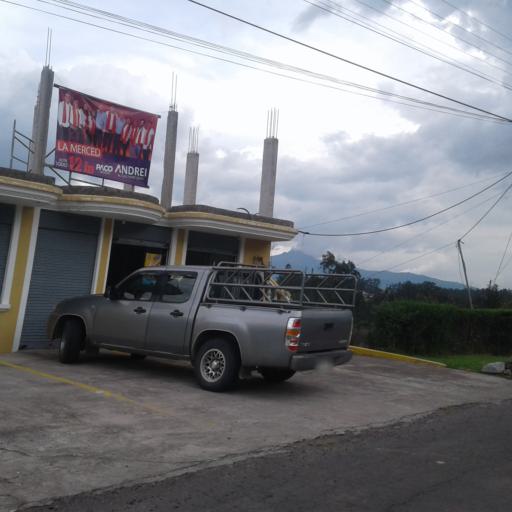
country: EC
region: Pichincha
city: Sangolqui
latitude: -0.2930
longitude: -78.3900
